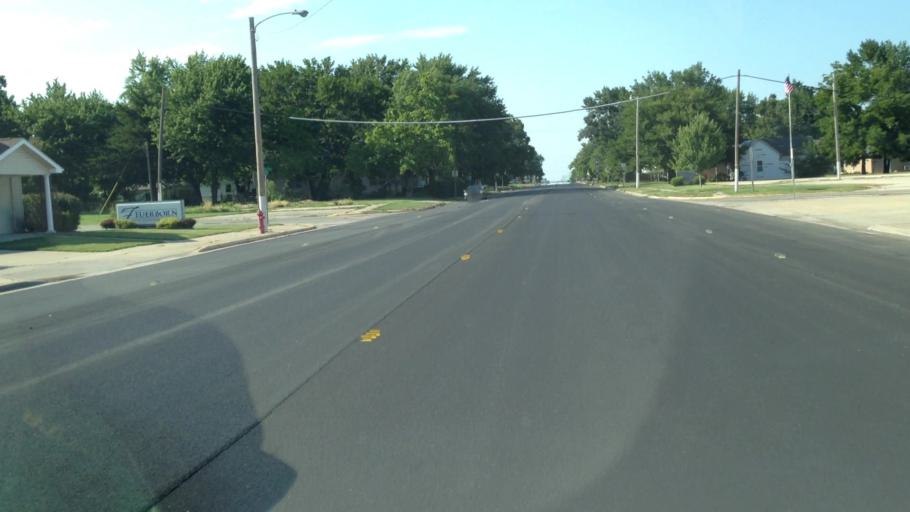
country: US
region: Kansas
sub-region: Allen County
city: Iola
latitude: 37.9162
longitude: -95.1701
